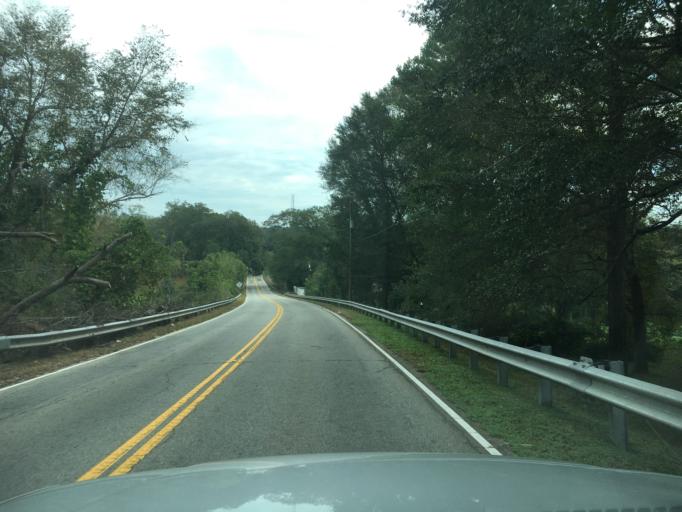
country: US
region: South Carolina
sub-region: Spartanburg County
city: Duncan
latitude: 34.9372
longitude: -82.1633
